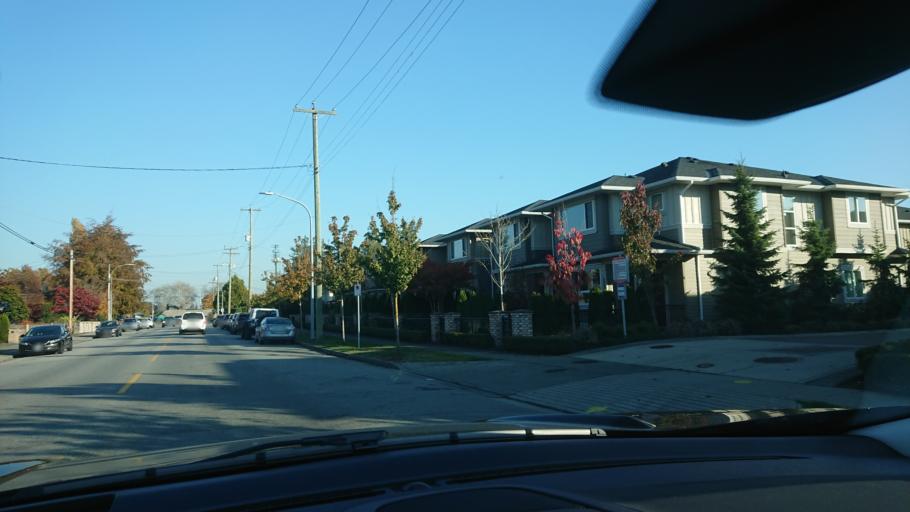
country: CA
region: British Columbia
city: Richmond
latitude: 49.1250
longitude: -123.1616
